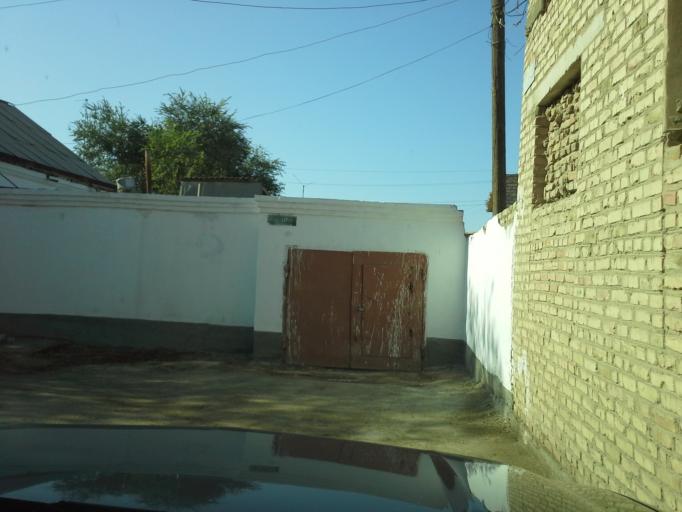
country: TM
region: Dasoguz
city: Dasoguz
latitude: 41.8298
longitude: 59.9749
